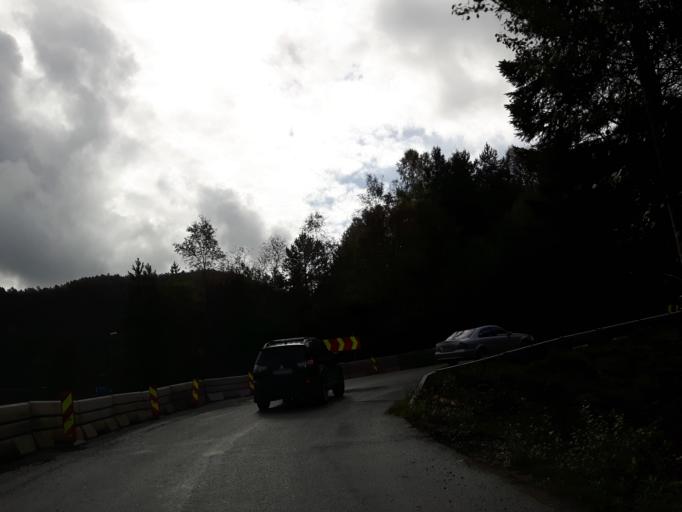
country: NO
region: Rogaland
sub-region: Lund
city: Moi
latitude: 58.3982
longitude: 6.6297
